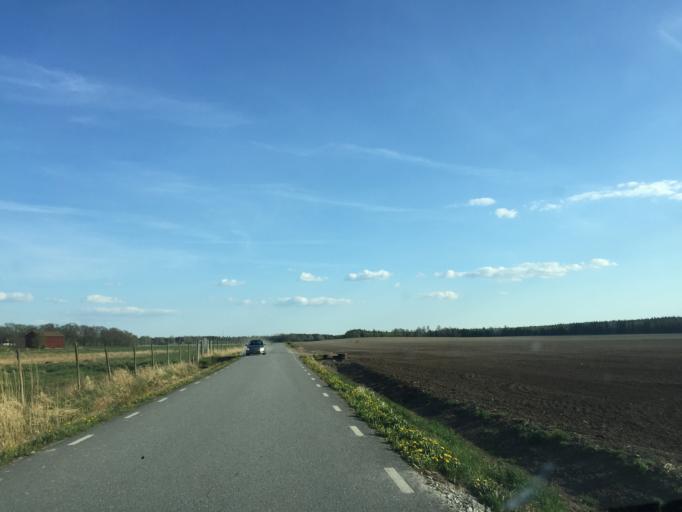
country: SE
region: OErebro
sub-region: Orebro Kommun
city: Hovsta
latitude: 59.3512
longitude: 15.1640
